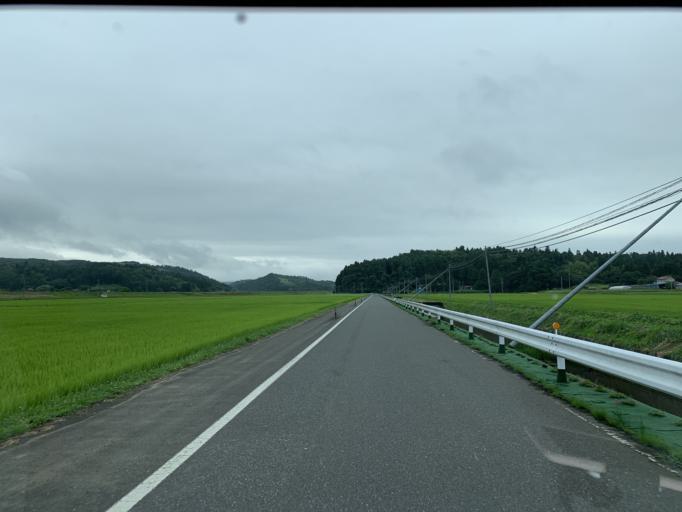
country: JP
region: Iwate
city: Ichinoseki
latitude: 38.8134
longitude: 141.2044
